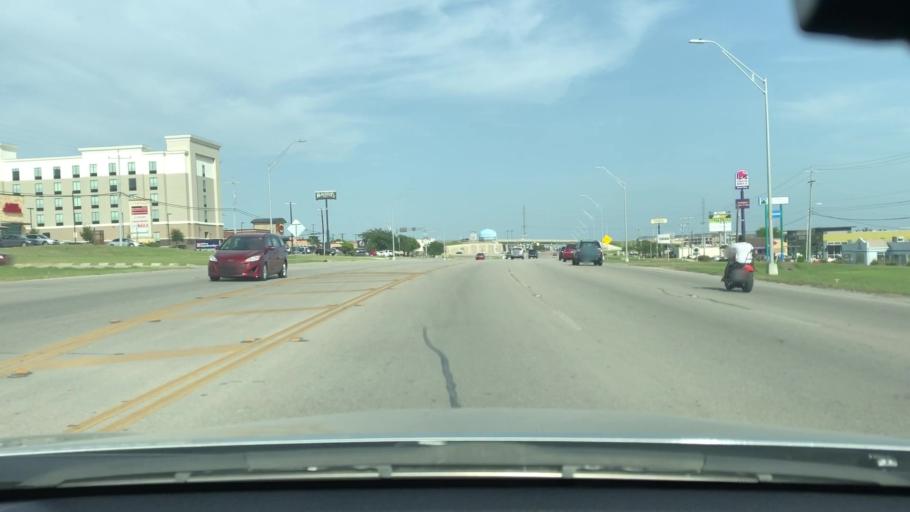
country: US
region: Texas
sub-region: Bexar County
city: Live Oak
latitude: 29.5629
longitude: -98.3329
